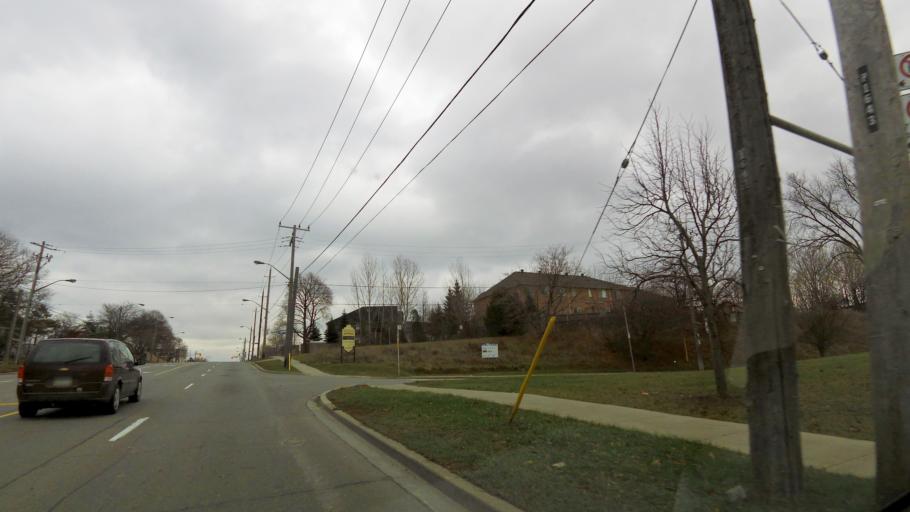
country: CA
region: Ontario
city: Concord
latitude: 43.7430
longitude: -79.4946
